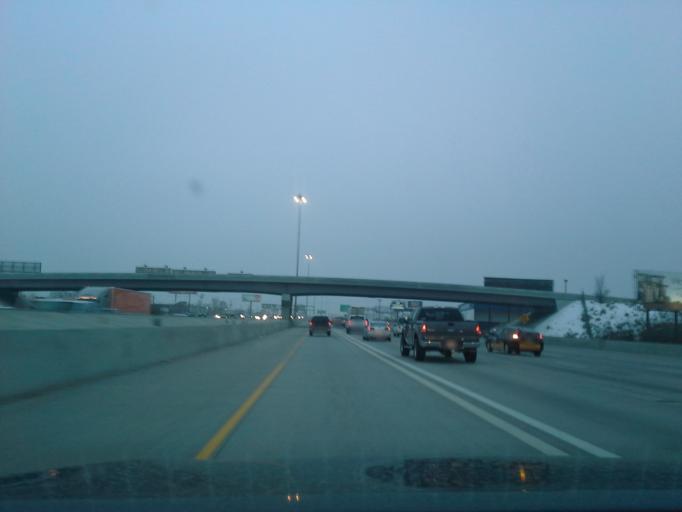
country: US
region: Utah
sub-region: Salt Lake County
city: South Salt Lake
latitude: 40.7138
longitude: -111.9043
